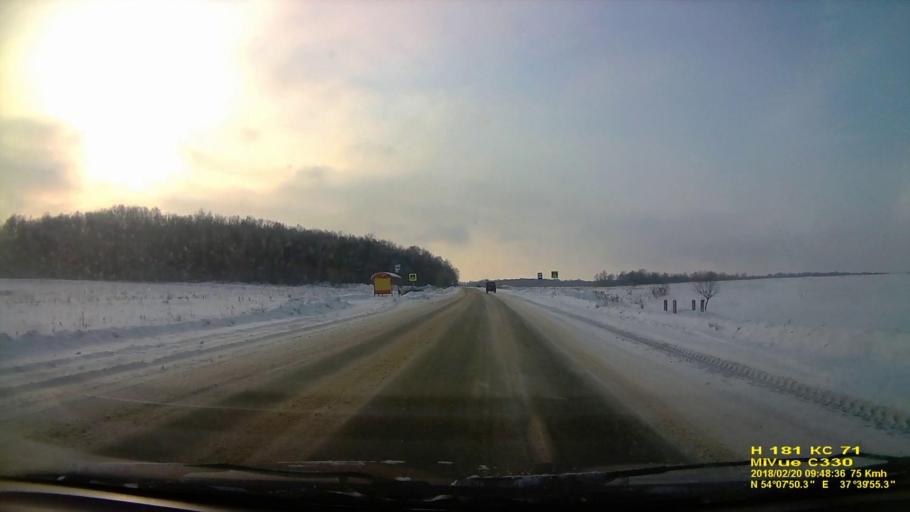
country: RU
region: Tula
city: Skuratovskiy
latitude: 54.1305
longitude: 37.6650
